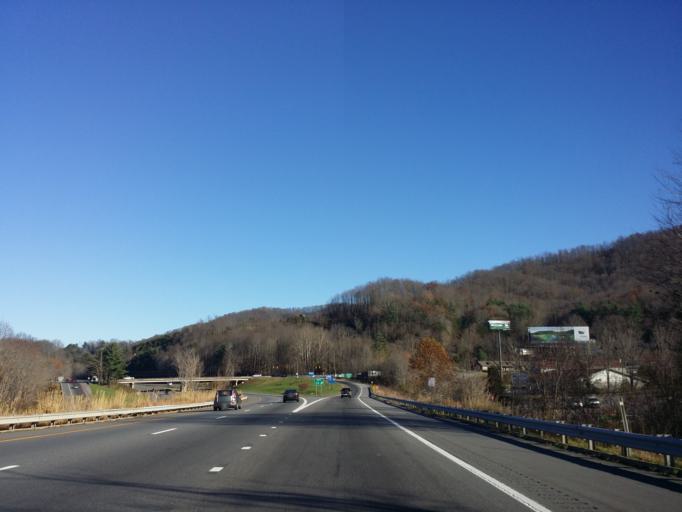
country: US
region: North Carolina
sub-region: Buncombe County
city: Swannanoa
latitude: 35.5949
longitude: -82.4074
